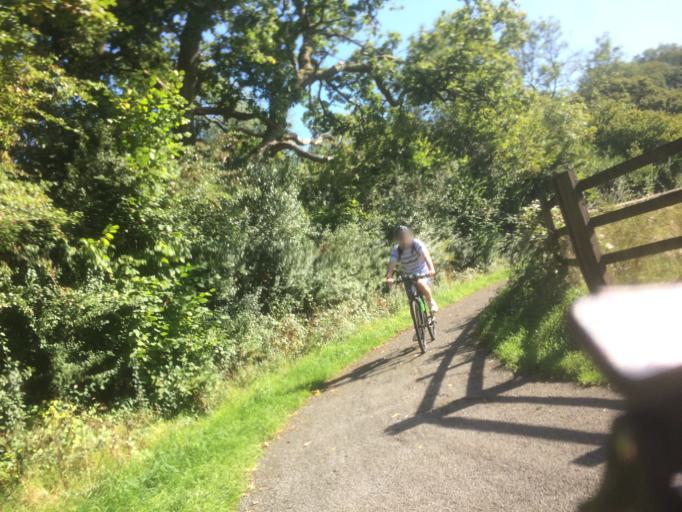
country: GB
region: England
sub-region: Devon
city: Tavistock
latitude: 50.5323
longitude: -4.1351
